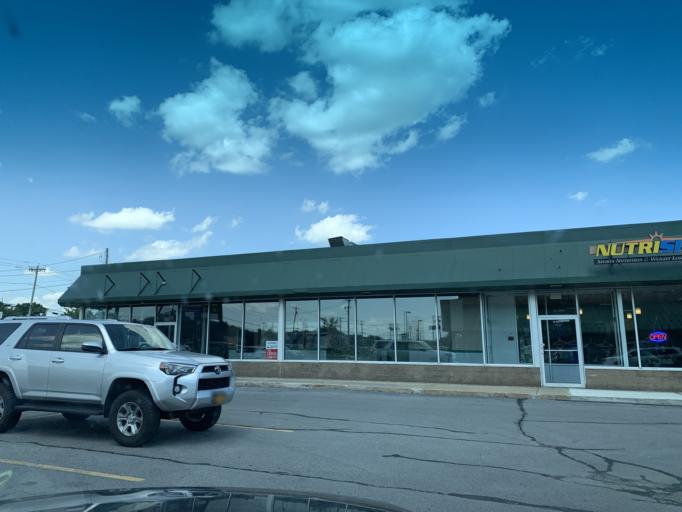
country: US
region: New York
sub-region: Oneida County
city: New York Mills
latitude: 43.0883
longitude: -75.3116
